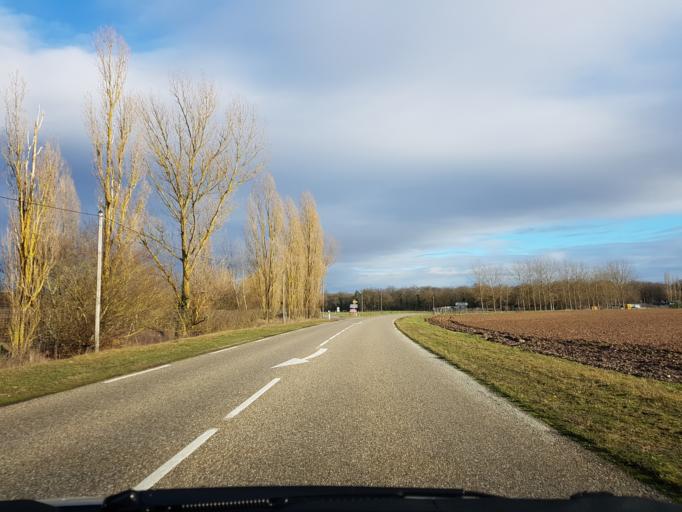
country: FR
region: Alsace
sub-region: Departement du Haut-Rhin
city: Habsheim
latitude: 47.7279
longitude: 7.4337
